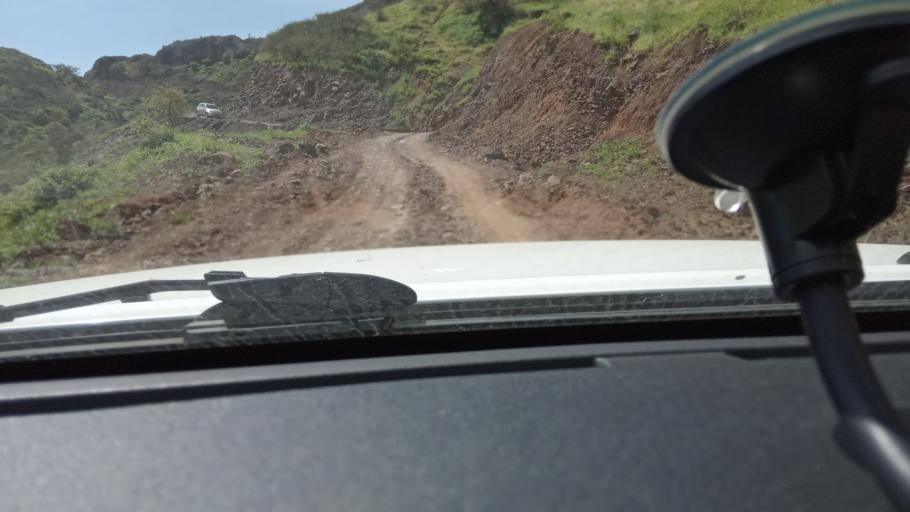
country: CV
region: Santa Catarina
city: Assomada
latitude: 15.0659
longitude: -23.6975
